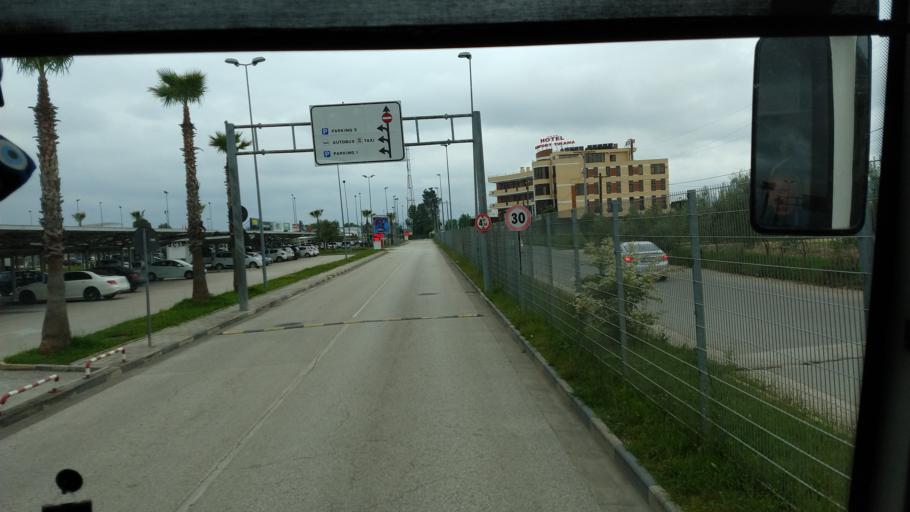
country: AL
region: Tirane
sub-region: Rrethi i Tiranes
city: Preze
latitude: 41.4180
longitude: 19.7128
